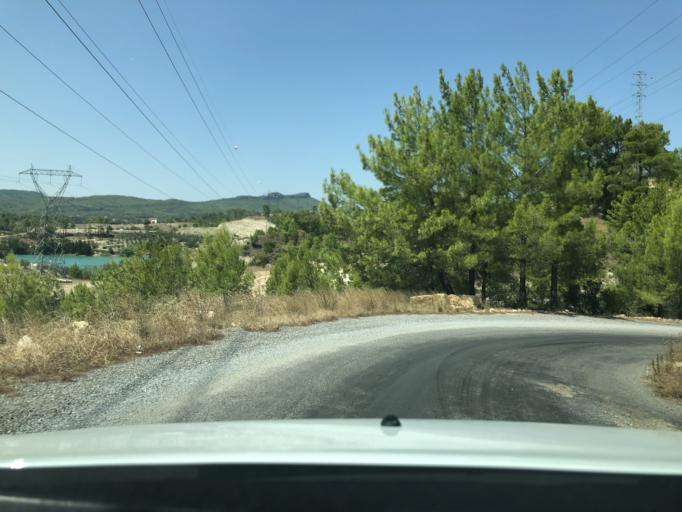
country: TR
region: Antalya
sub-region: Manavgat
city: Manavgat
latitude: 36.8766
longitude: 31.5475
